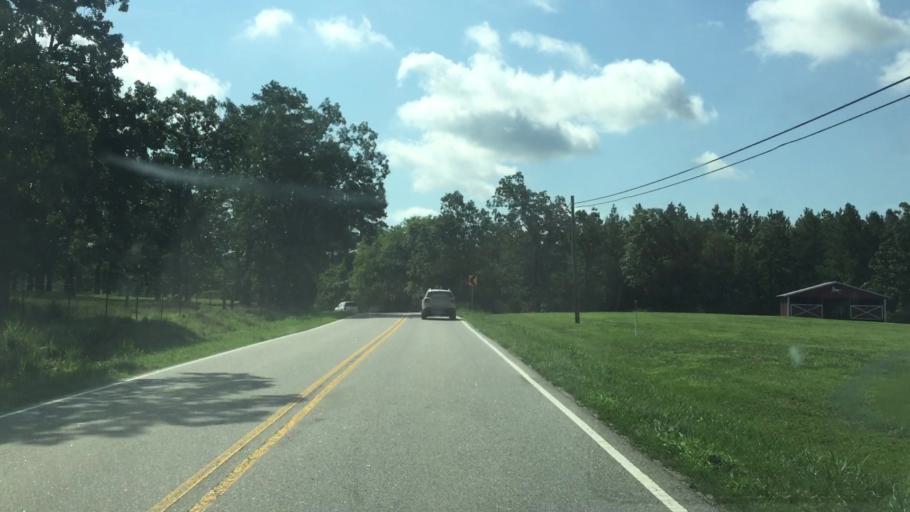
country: US
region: North Carolina
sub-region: Anson County
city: Polkton
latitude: 35.0322
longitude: -80.2428
